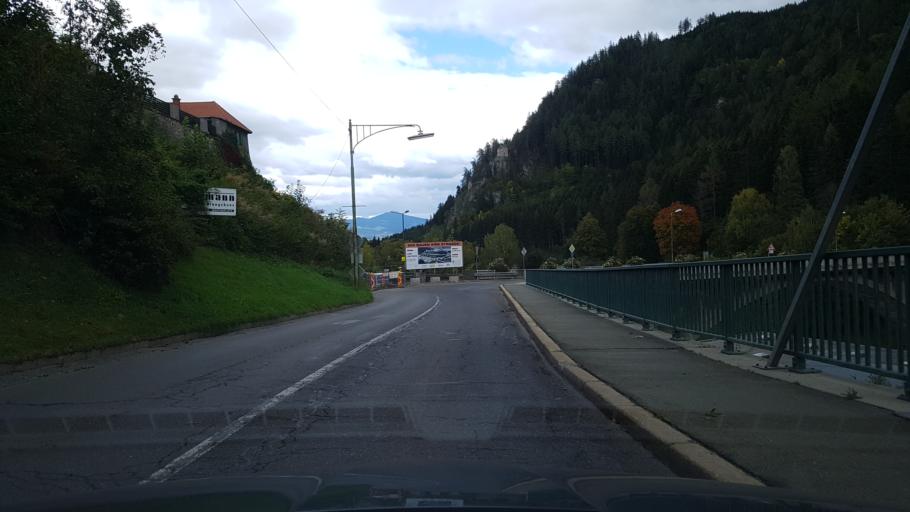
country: AT
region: Styria
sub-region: Politischer Bezirk Murtal
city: Judenburg
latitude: 47.1681
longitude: 14.6658
